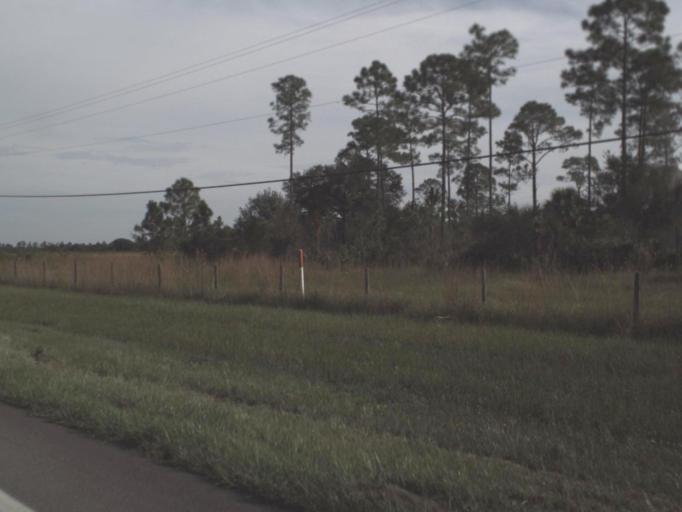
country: US
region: Florida
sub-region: Lee County
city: Olga
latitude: 26.8232
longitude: -81.7601
